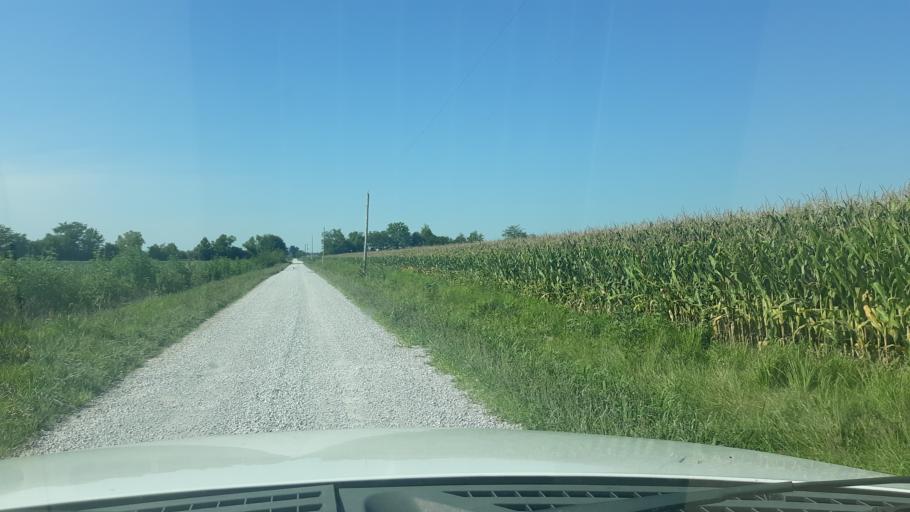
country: US
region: Illinois
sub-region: Saline County
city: Eldorado
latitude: 37.8484
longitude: -88.4849
